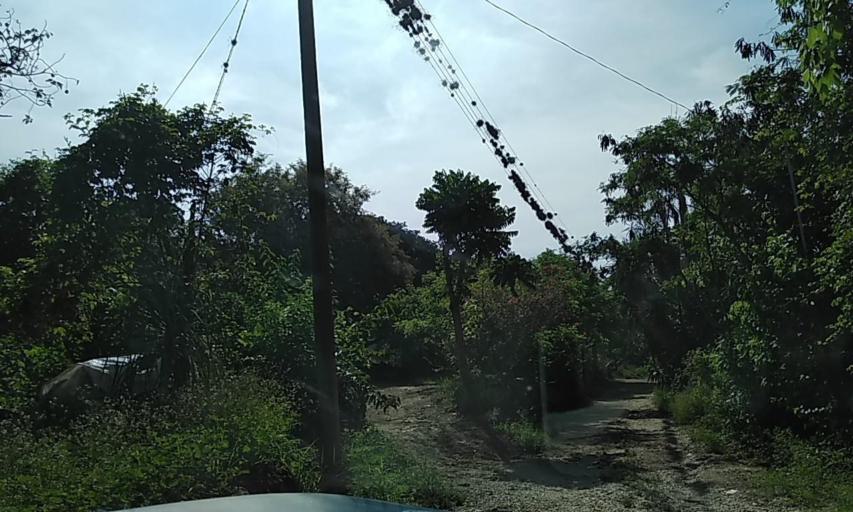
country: MX
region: Veracruz
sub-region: Emiliano Zapata
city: Plan del Rio
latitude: 19.4537
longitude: -96.6786
